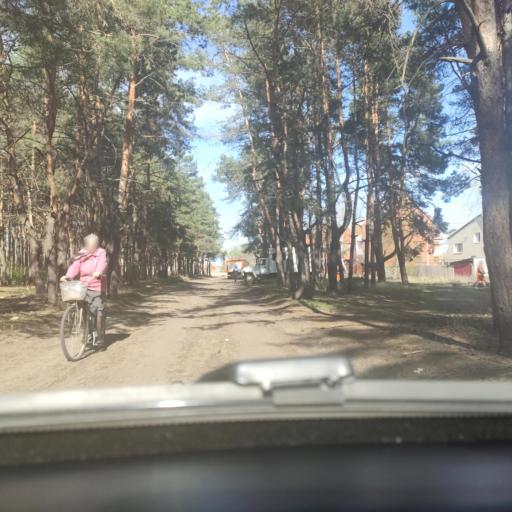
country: RU
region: Voronezj
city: Somovo
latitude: 51.7478
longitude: 39.3248
